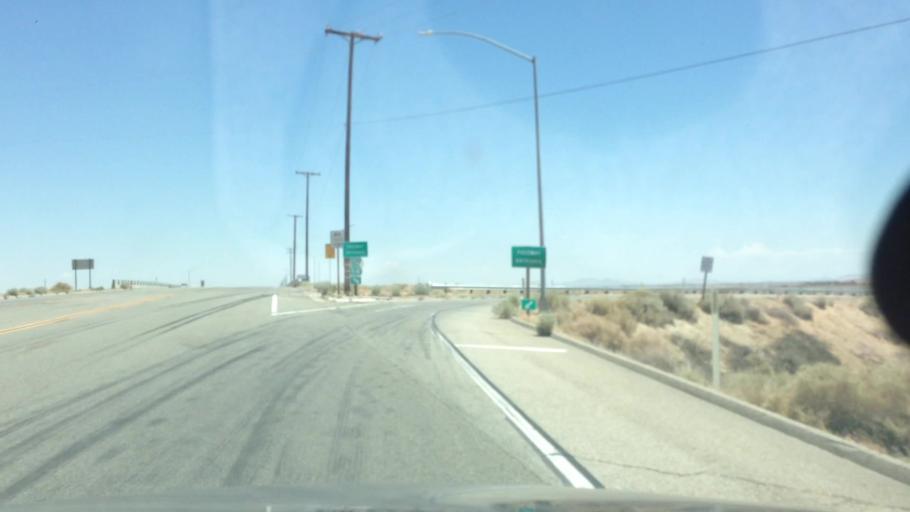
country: US
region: California
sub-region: Los Angeles County
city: Lancaster
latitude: 34.7768
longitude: -118.1724
